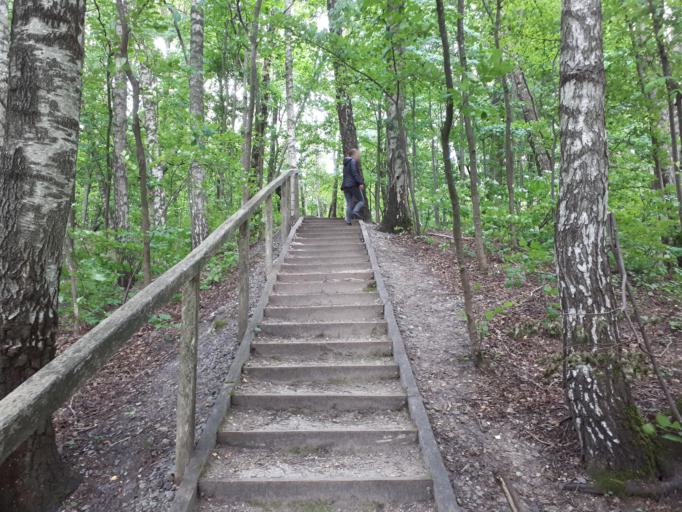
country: LT
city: Ramuciai
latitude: 54.8876
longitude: 24.0731
